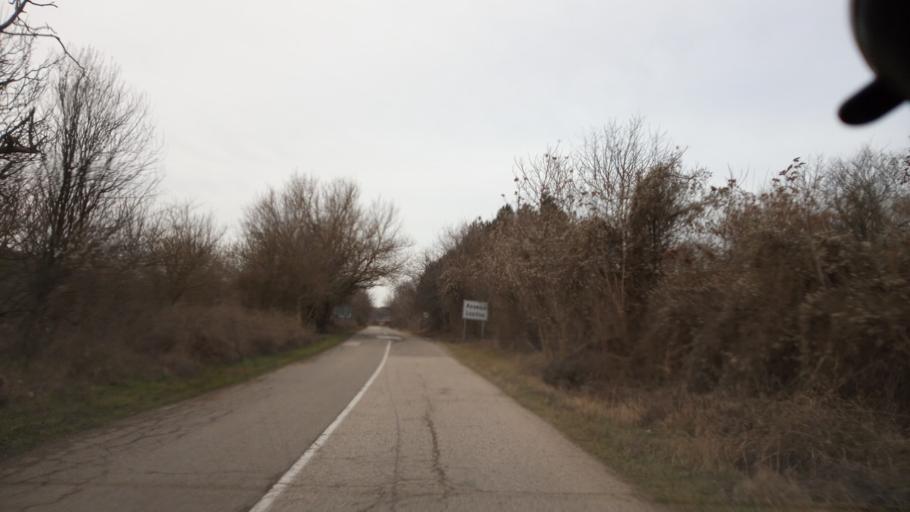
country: BG
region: Pleven
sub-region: Obshtina Belene
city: Belene
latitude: 43.6122
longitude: 25.0191
